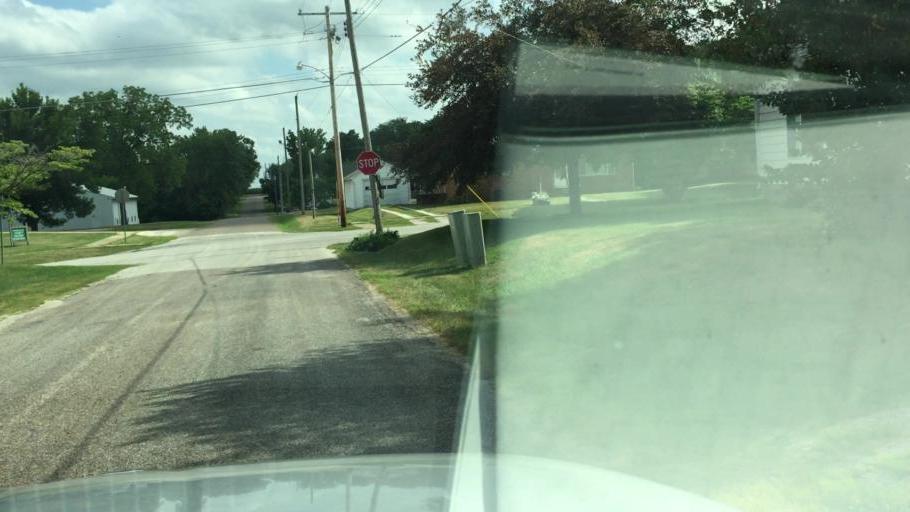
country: US
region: Illinois
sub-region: Hancock County
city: Carthage
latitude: 40.4126
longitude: -91.1276
